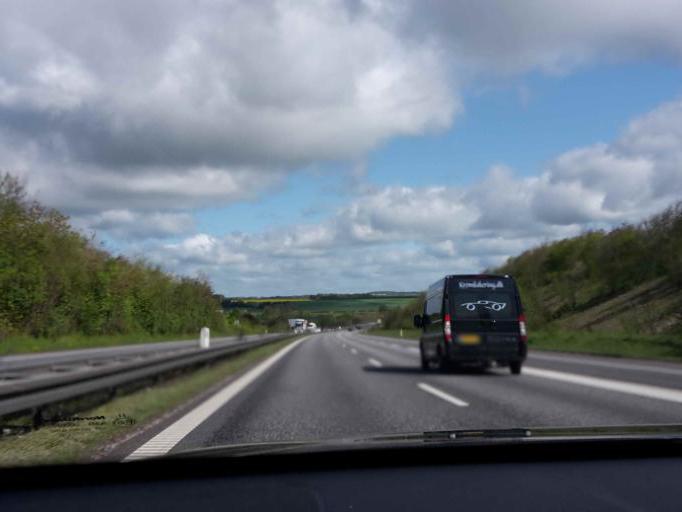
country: DK
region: Central Jutland
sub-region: Skanderborg Kommune
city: Horning
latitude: 56.1250
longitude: 10.0351
